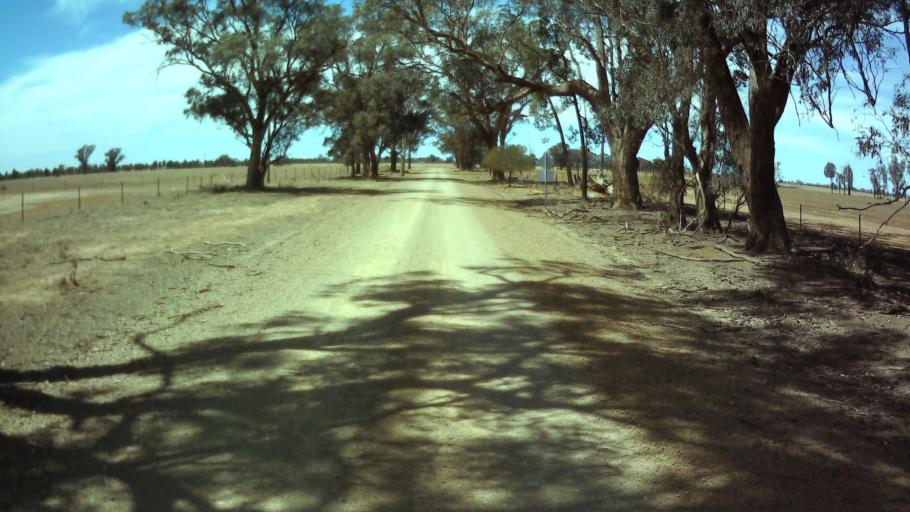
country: AU
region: New South Wales
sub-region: Weddin
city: Grenfell
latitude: -33.8616
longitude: 147.8064
